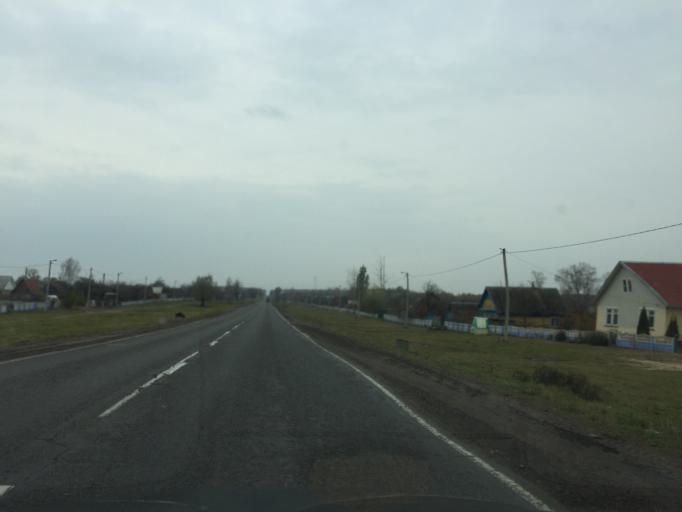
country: BY
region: Gomel
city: Dowsk
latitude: 53.1650
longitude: 30.4777
